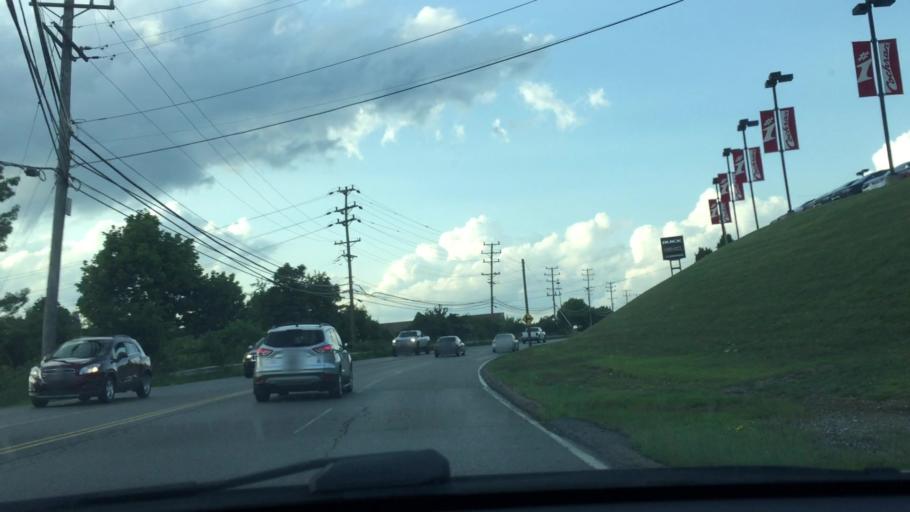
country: US
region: Pennsylvania
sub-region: Allegheny County
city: Rennerdale
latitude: 40.4444
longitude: -80.1589
